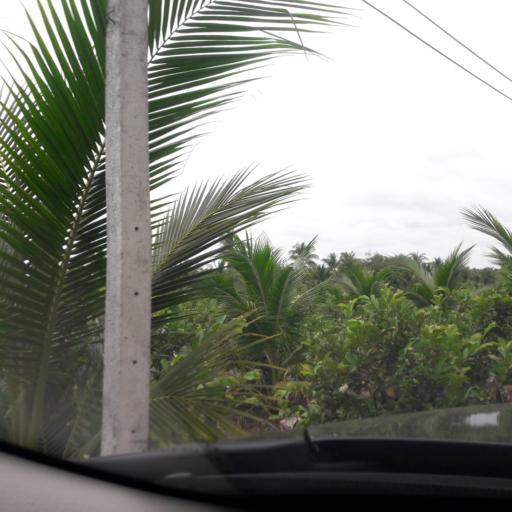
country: TH
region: Ratchaburi
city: Damnoen Saduak
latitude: 13.5723
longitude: 99.9451
